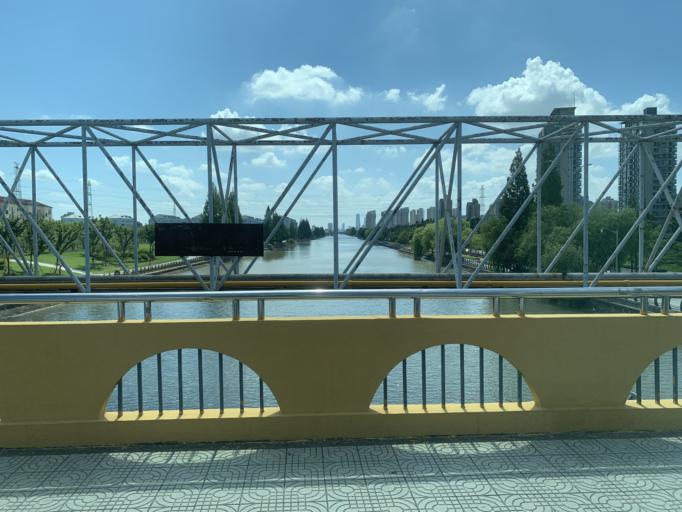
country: CN
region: Shanghai Shi
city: Huamu
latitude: 31.1761
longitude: 121.5348
